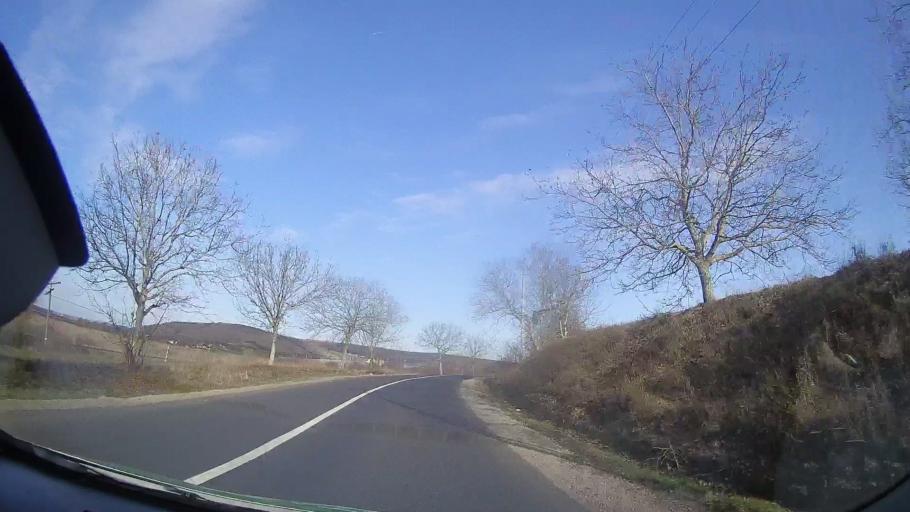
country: RO
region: Mures
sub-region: Comuna Zau De Campie
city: Zau de Campie
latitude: 46.5893
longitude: 24.1042
